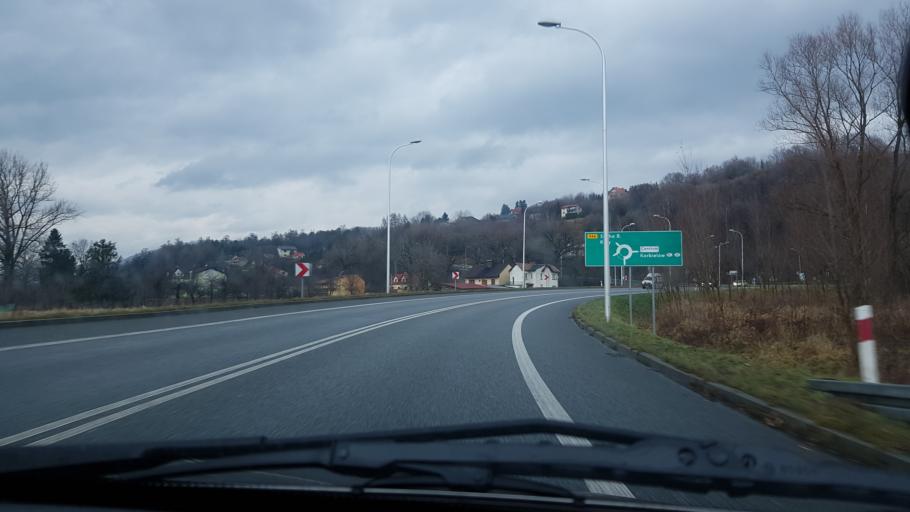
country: PL
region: Silesian Voivodeship
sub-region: Powiat zywiecki
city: Zywiec
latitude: 49.6996
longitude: 19.1991
